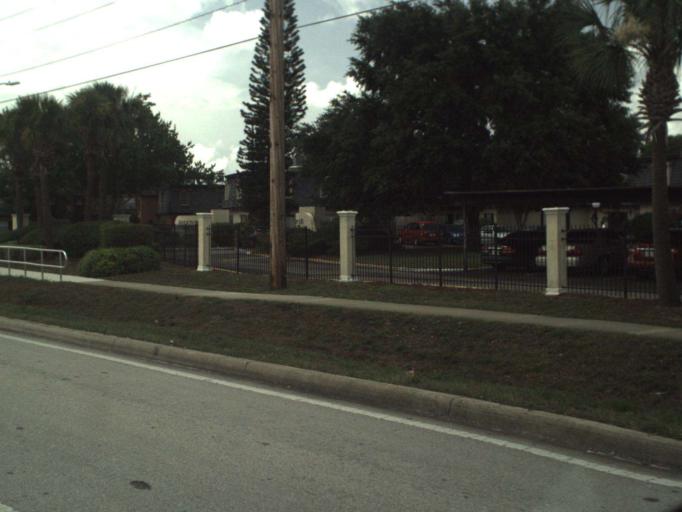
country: US
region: Florida
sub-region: Seminole County
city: Goldenrod
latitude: 28.6209
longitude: -81.3136
